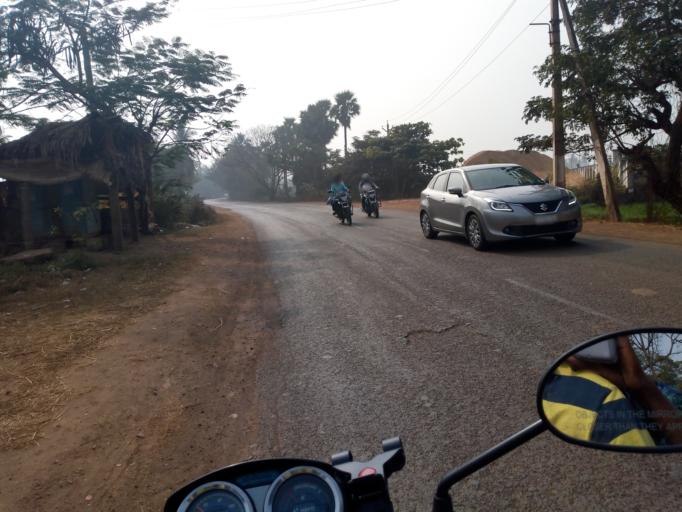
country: IN
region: Andhra Pradesh
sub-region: West Godavari
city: Tadepallegudem
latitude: 16.8088
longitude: 81.4086
